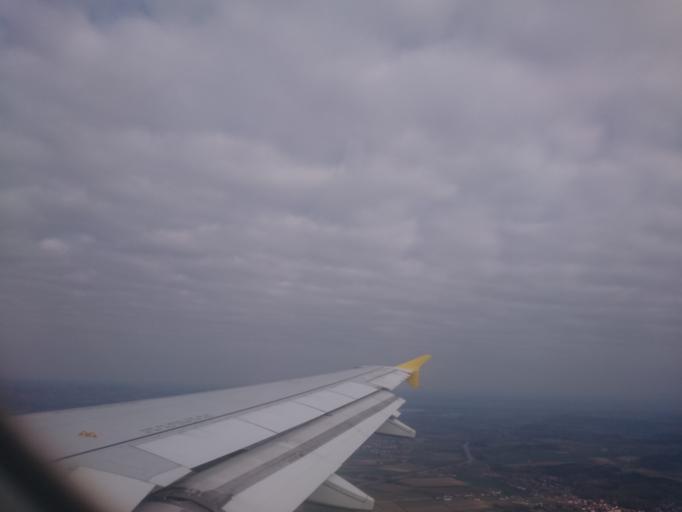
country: DE
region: Bavaria
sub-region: Upper Bavaria
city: Fraunberg
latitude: 48.3783
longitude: 11.9711
